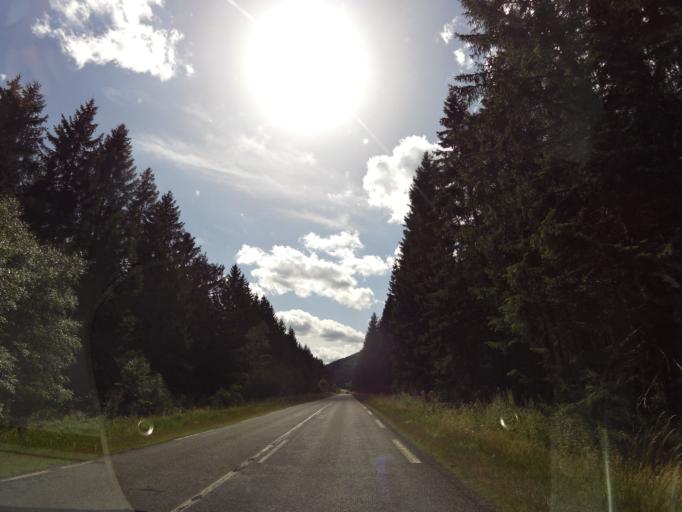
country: FR
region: Auvergne
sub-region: Departement du Puy-de-Dome
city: Orcines
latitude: 45.7550
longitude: 2.9726
